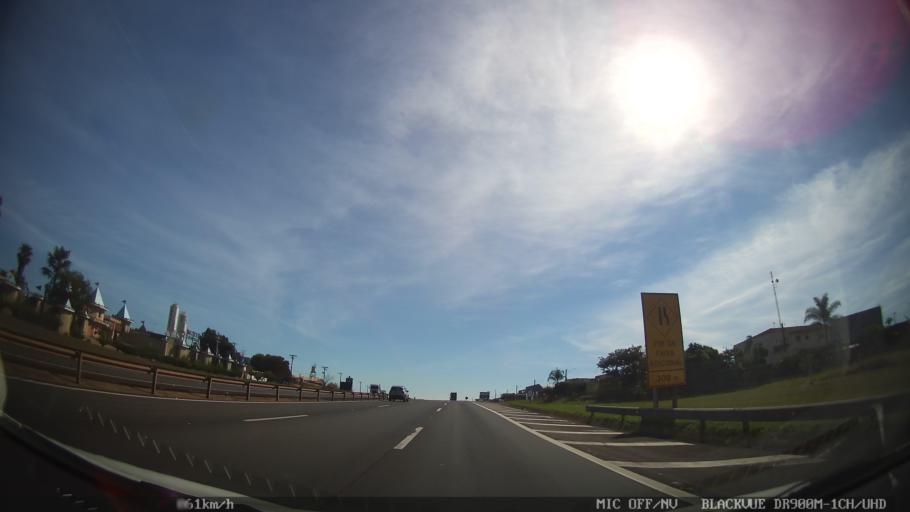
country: BR
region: Sao Paulo
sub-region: Pirassununga
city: Pirassununga
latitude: -22.0371
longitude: -47.4324
